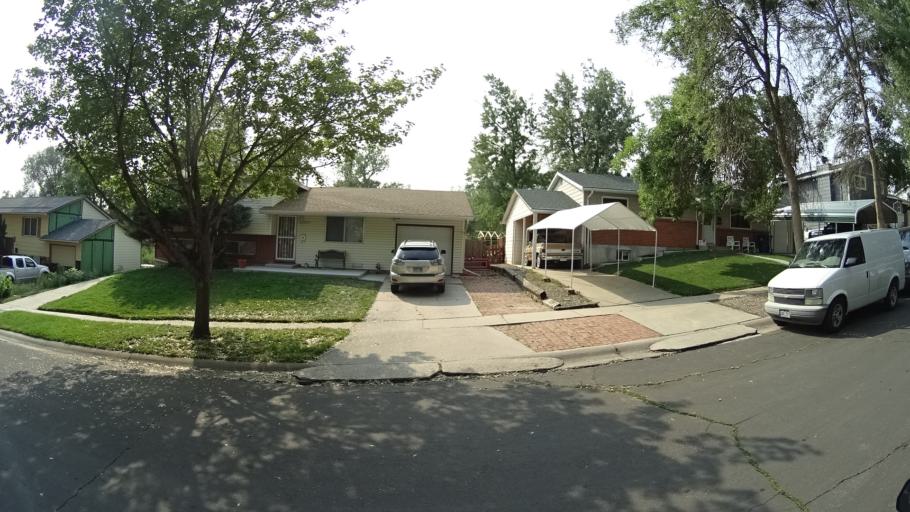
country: US
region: Colorado
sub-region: El Paso County
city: Stratmoor
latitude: 38.8101
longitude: -104.7768
